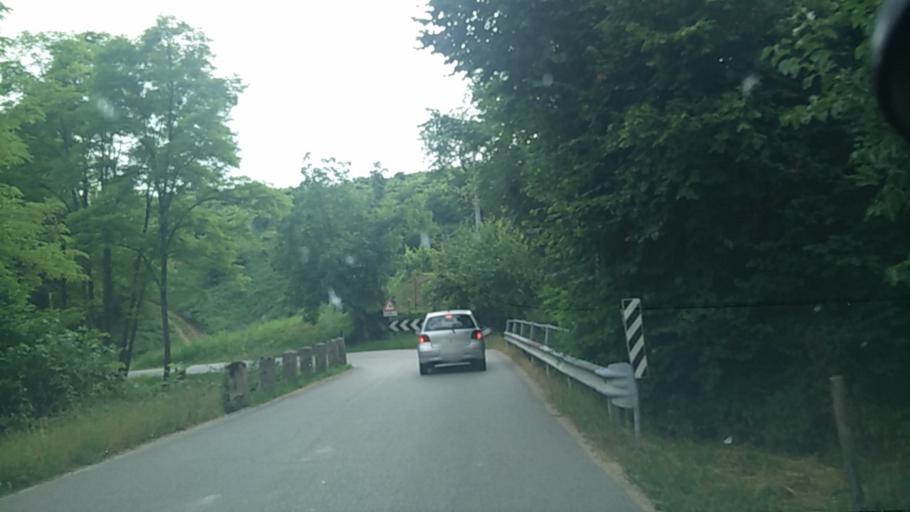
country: IT
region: Veneto
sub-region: Provincia di Treviso
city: Miane
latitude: 45.9140
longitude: 12.0770
